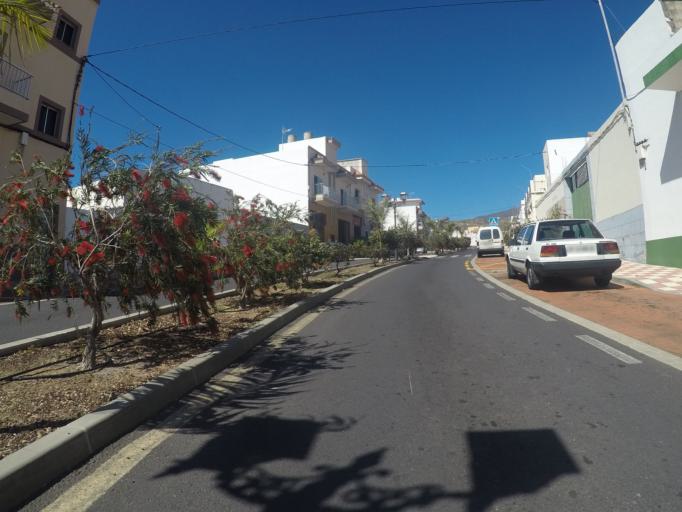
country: ES
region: Canary Islands
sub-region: Provincia de Santa Cruz de Tenerife
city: Lomo de Arico
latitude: 28.1821
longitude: -16.4811
